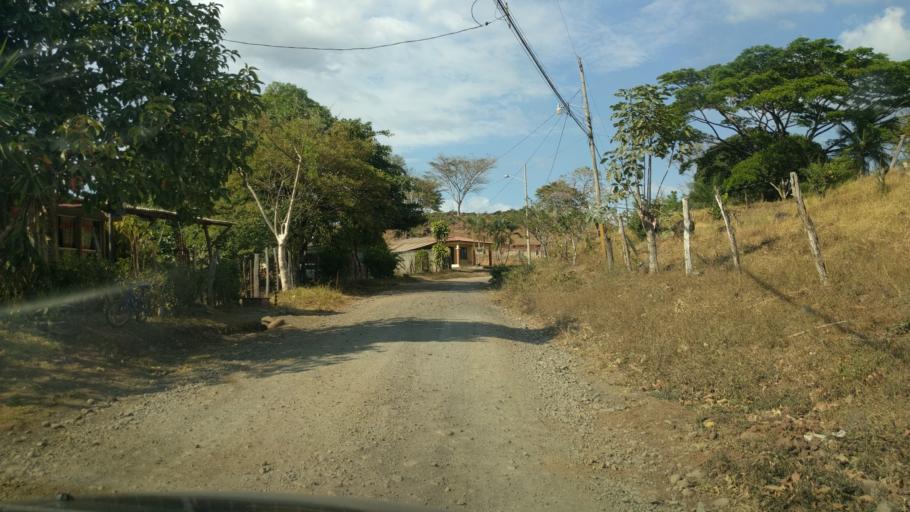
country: CR
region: Puntarenas
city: Esparza
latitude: 10.0150
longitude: -84.6909
